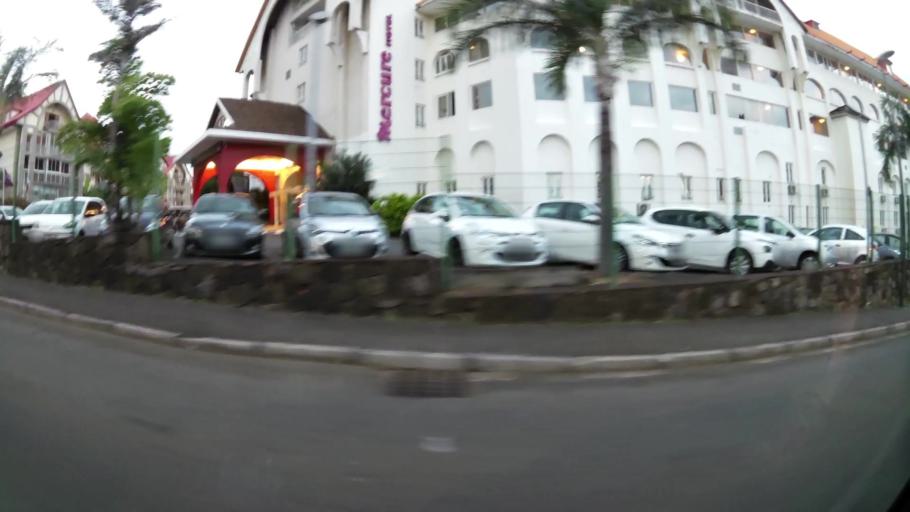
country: RE
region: Reunion
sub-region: Reunion
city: Saint-Denis
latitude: -20.9011
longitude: 55.4682
